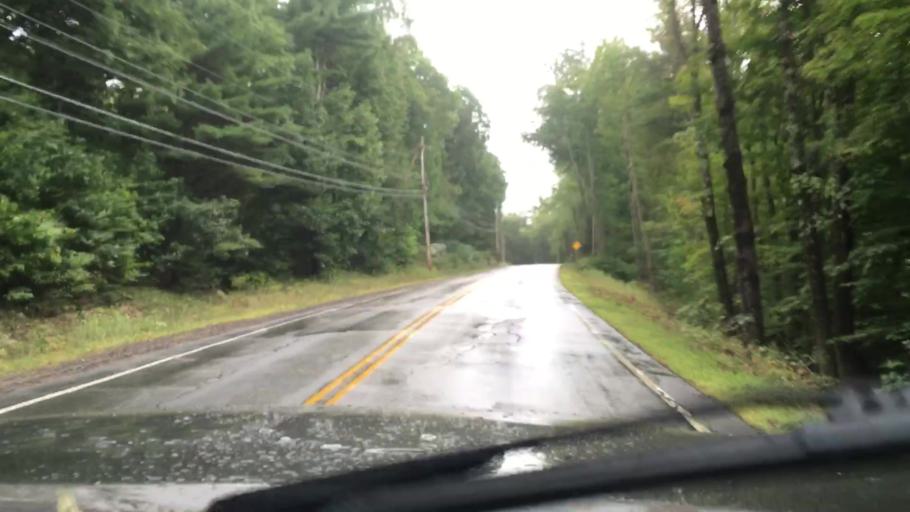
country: US
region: New Hampshire
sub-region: Belknap County
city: Meredith
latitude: 43.6493
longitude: -71.5422
